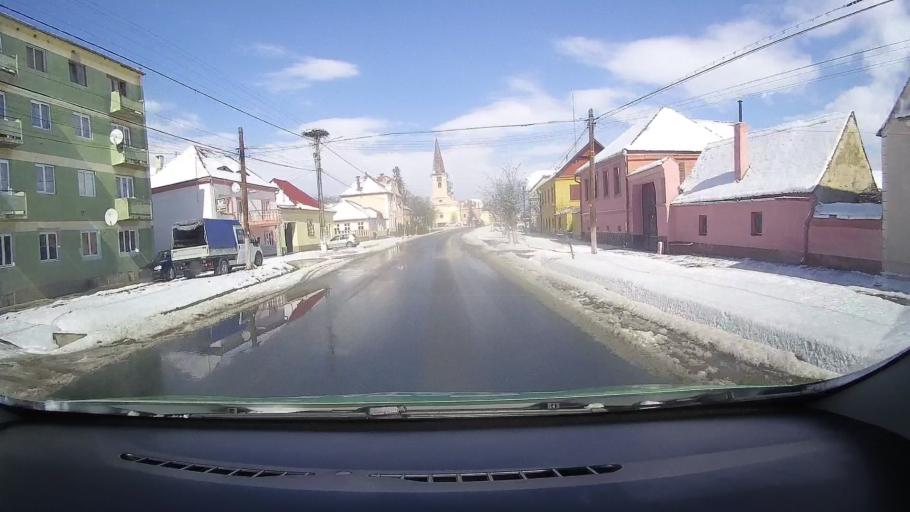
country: RO
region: Sibiu
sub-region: Comuna Nocrich
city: Nocrich
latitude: 45.8936
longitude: 24.4541
